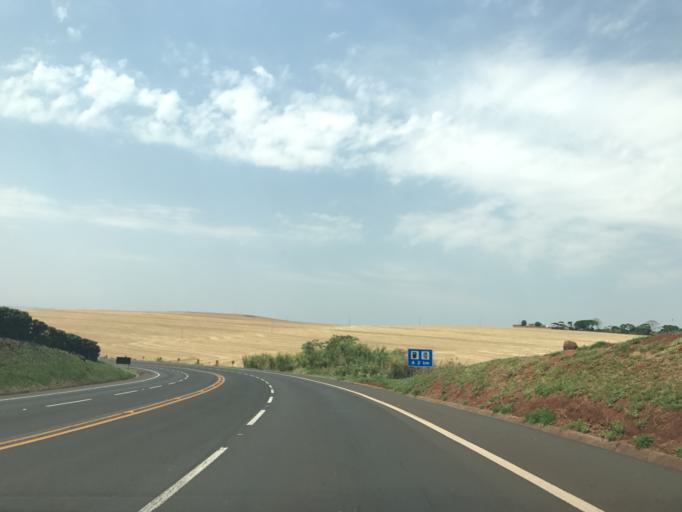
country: BR
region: Parana
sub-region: Mandaguari
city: Mandaguari
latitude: -23.4782
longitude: -51.5866
